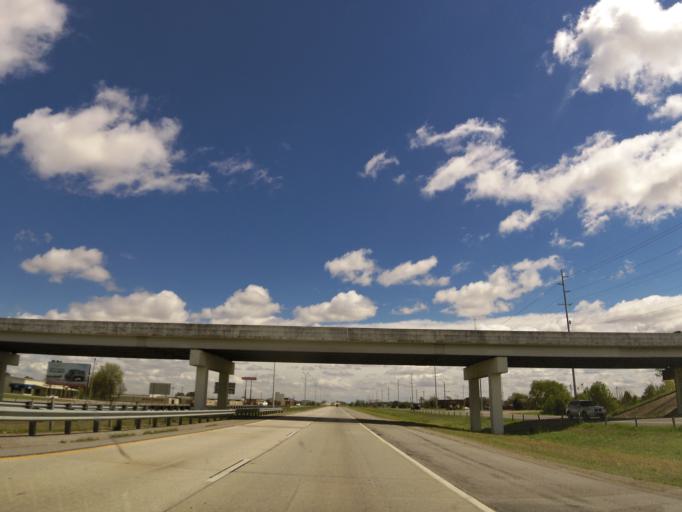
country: US
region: Arkansas
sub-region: Craighead County
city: Jonesboro
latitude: 35.8069
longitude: -90.6520
